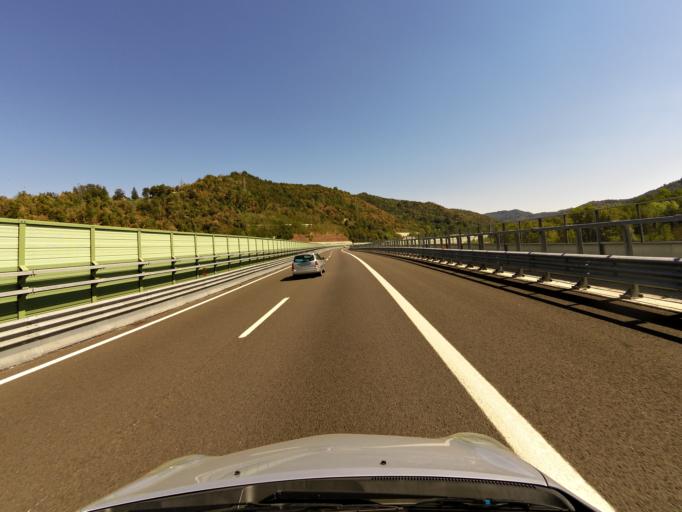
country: IT
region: Emilia-Romagna
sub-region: Provincia di Bologna
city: Marzabotto
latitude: 44.2899
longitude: 11.2096
